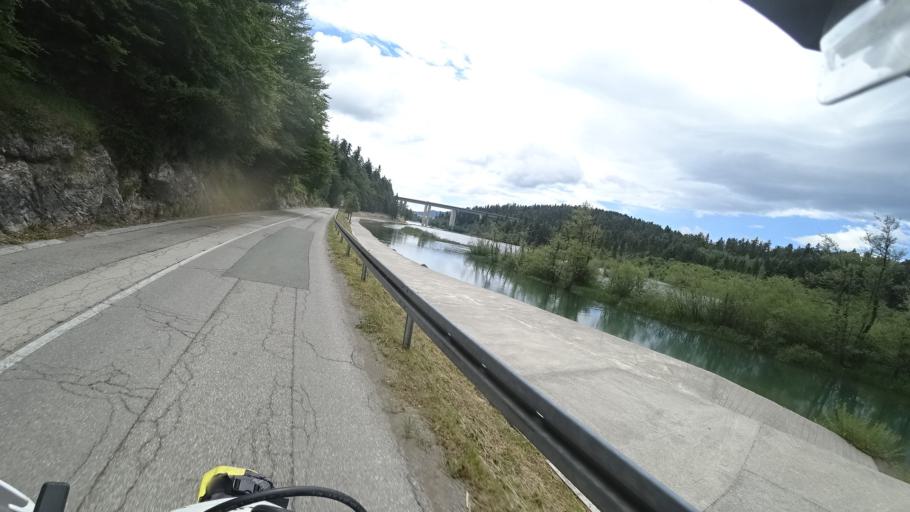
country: HR
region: Primorsko-Goranska
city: Hreljin
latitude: 45.3224
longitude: 14.7067
